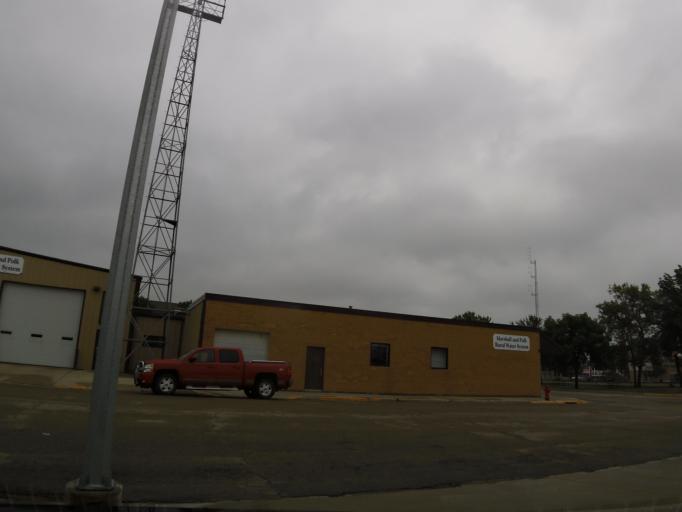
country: US
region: Minnesota
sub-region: Marshall County
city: Warren
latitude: 48.1956
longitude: -96.7729
